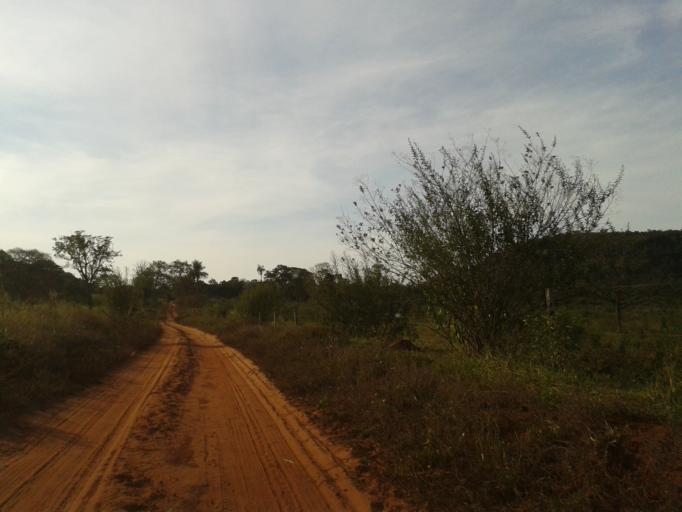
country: BR
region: Minas Gerais
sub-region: Campina Verde
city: Campina Verde
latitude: -19.5011
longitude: -49.6049
